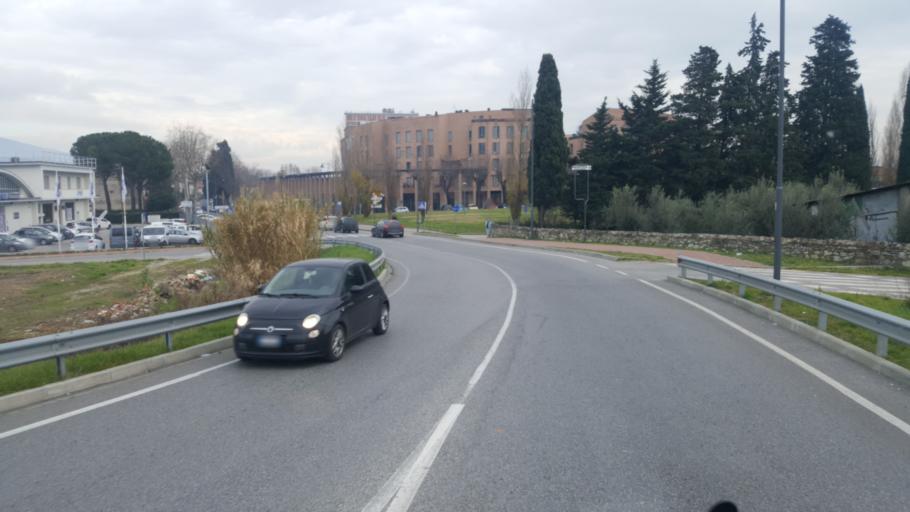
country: IT
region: Tuscany
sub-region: Province of Florence
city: Calenzano
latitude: 43.8583
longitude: 11.1451
